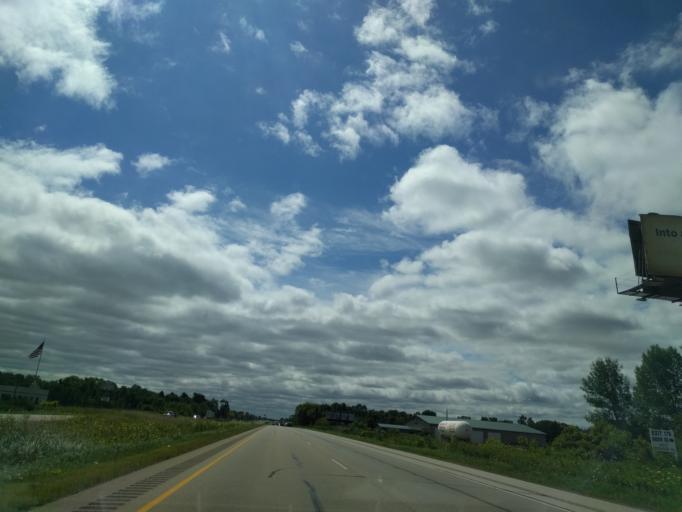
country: US
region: Wisconsin
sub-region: Brown County
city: Suamico
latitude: 44.7048
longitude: -88.0509
